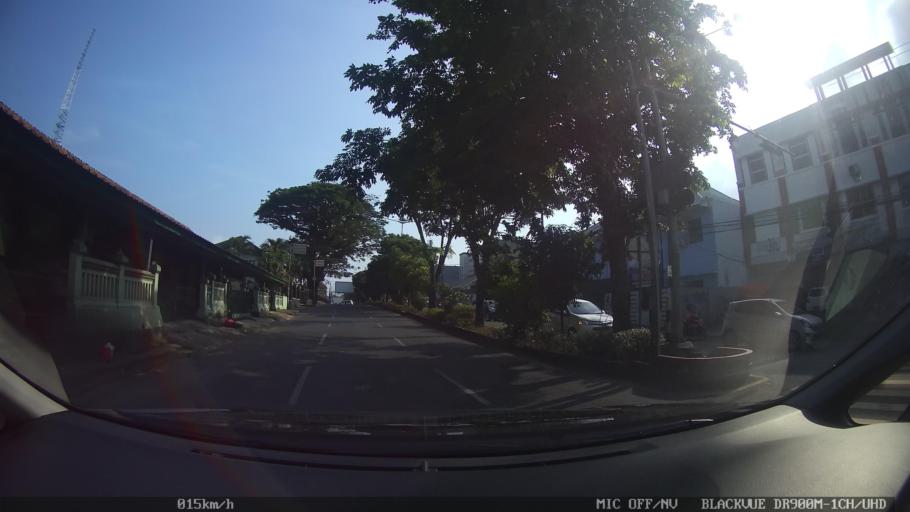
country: ID
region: Lampung
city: Kedaton
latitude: -5.4026
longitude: 105.2603
